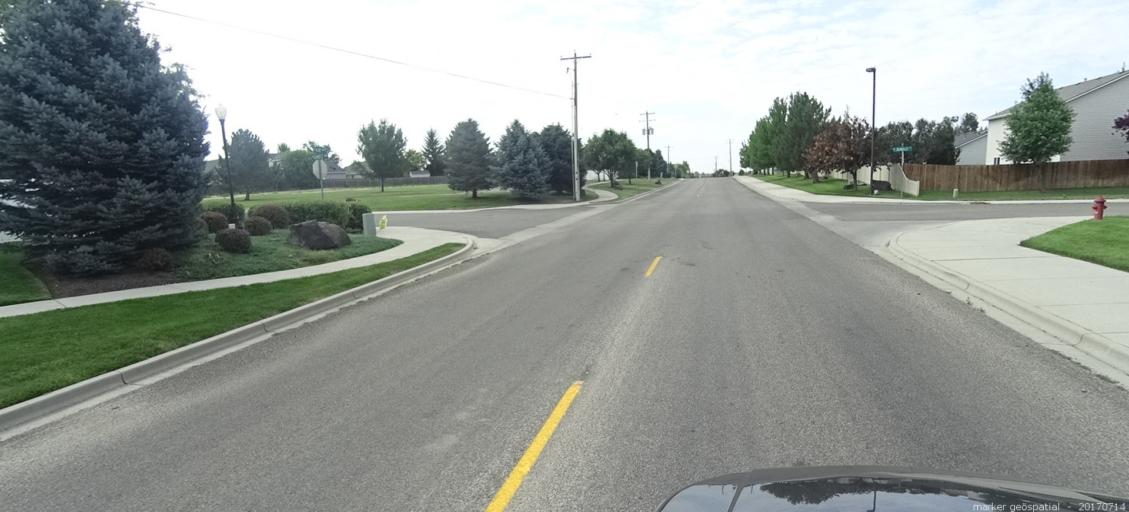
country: US
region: Idaho
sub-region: Ada County
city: Kuna
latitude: 43.4935
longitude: -116.4040
